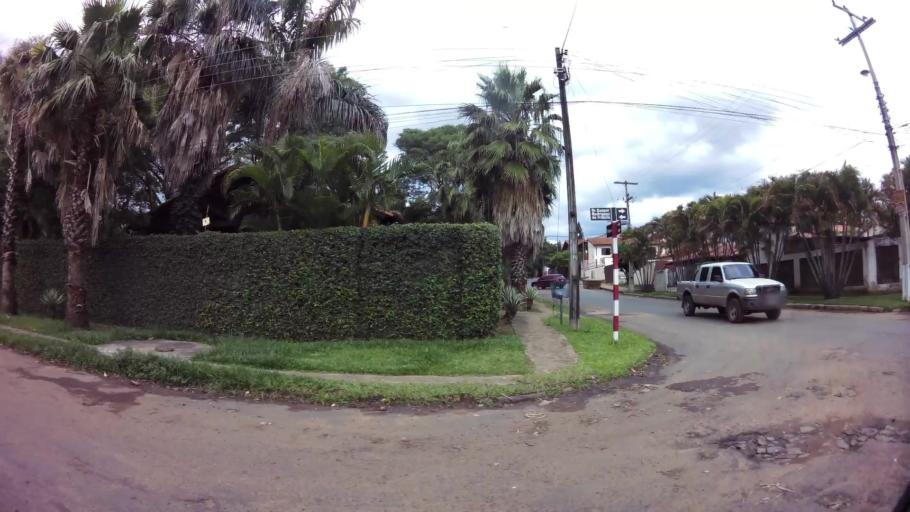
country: PY
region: Central
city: San Lorenzo
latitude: -25.2774
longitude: -57.4954
